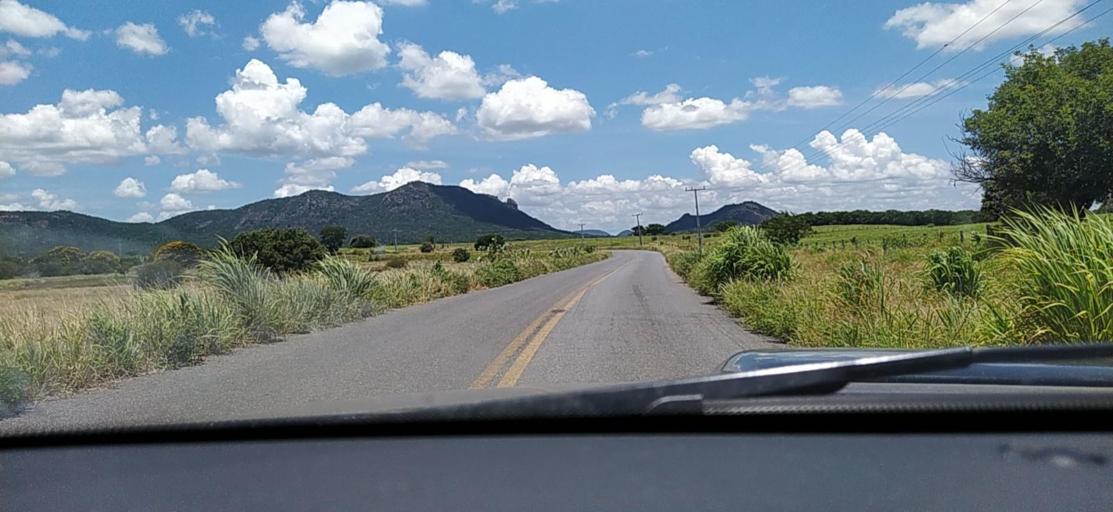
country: BR
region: Bahia
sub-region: Guanambi
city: Guanambi
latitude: -14.1588
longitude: -42.8181
